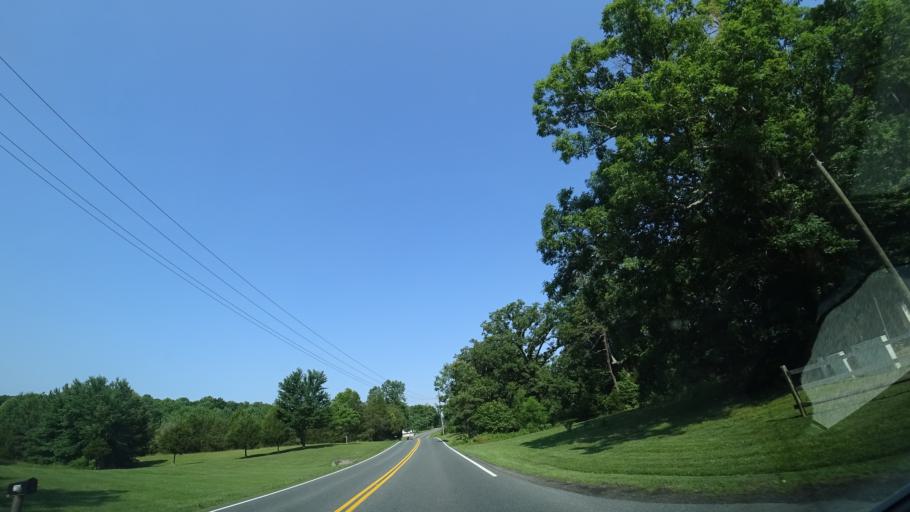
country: US
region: Virginia
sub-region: Louisa County
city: Louisa
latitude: 38.0832
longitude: -77.8383
